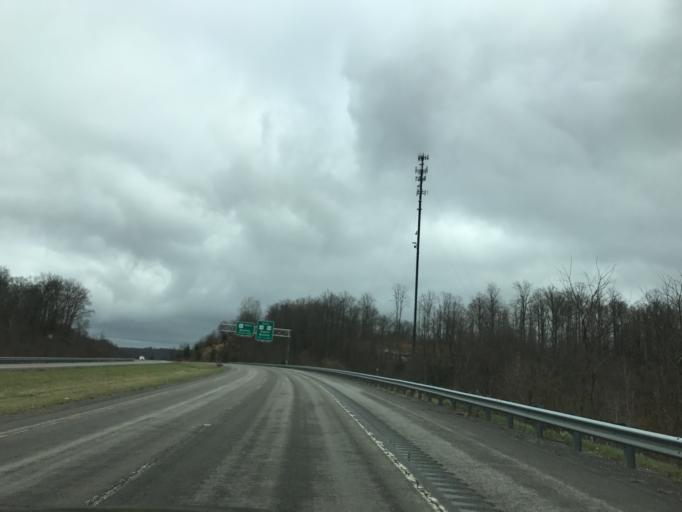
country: US
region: West Virginia
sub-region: Raleigh County
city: Sophia
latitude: 37.7129
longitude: -81.2662
